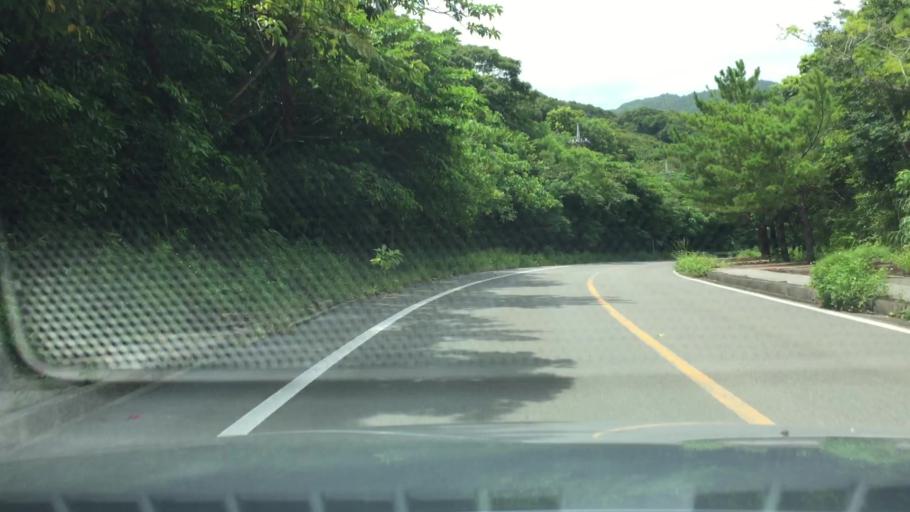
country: JP
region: Okinawa
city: Ishigaki
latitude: 24.4270
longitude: 124.2109
